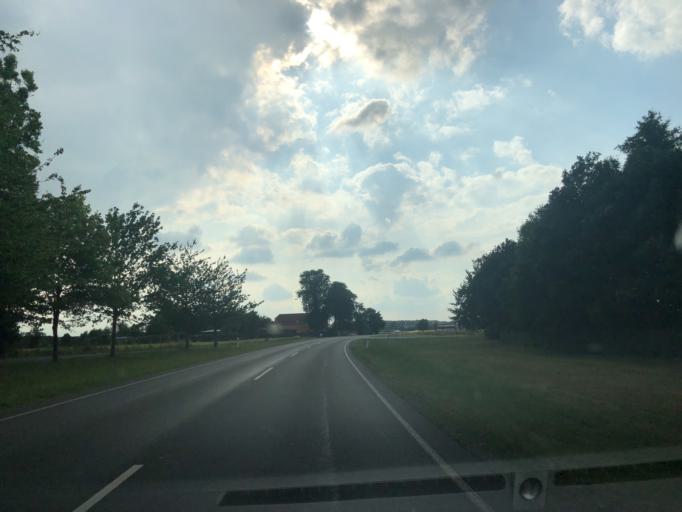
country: DK
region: Zealand
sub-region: Faxe Kommune
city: Fakse
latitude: 55.3140
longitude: 12.1423
